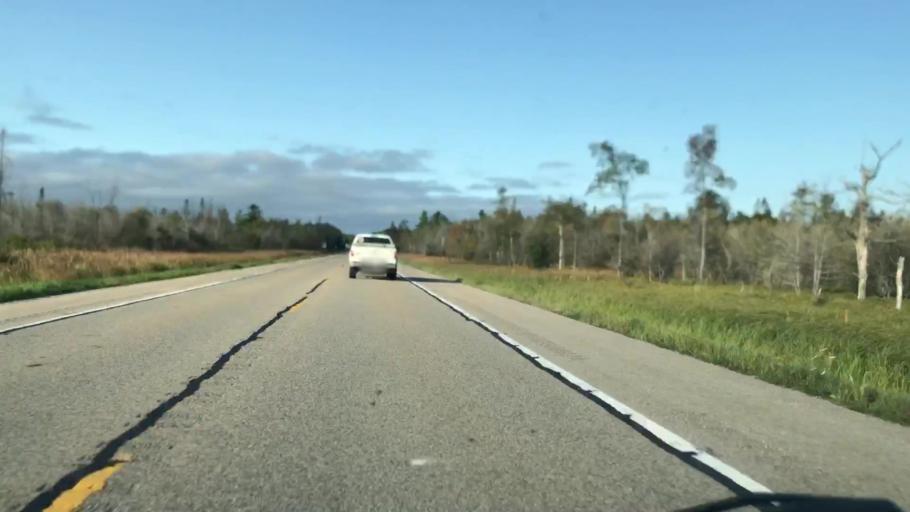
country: US
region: Michigan
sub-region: Luce County
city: Newberry
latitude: 46.3156
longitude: -85.1996
